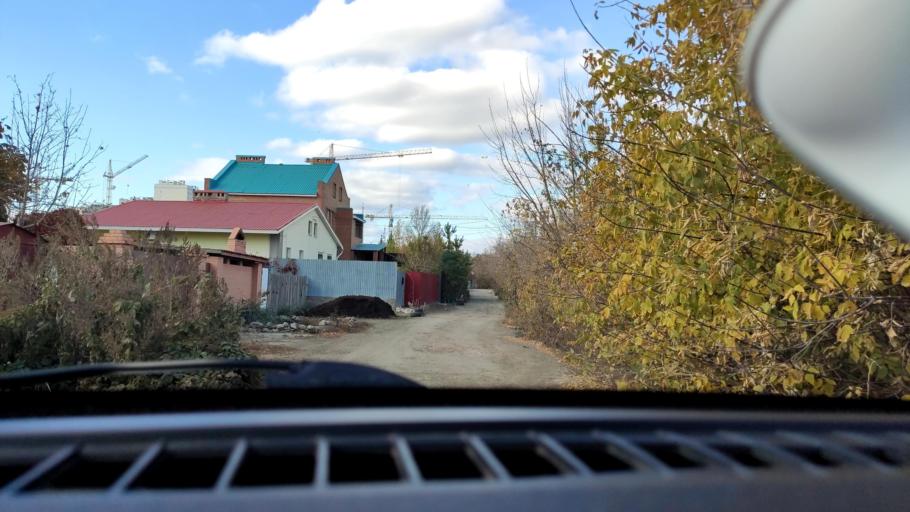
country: RU
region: Samara
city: Samara
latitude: 53.2213
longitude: 50.2093
